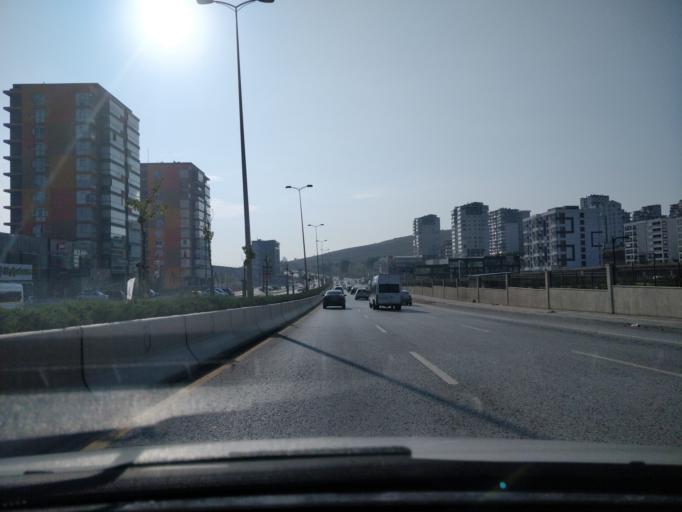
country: TR
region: Ankara
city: Etimesgut
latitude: 39.8969
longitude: 32.6540
